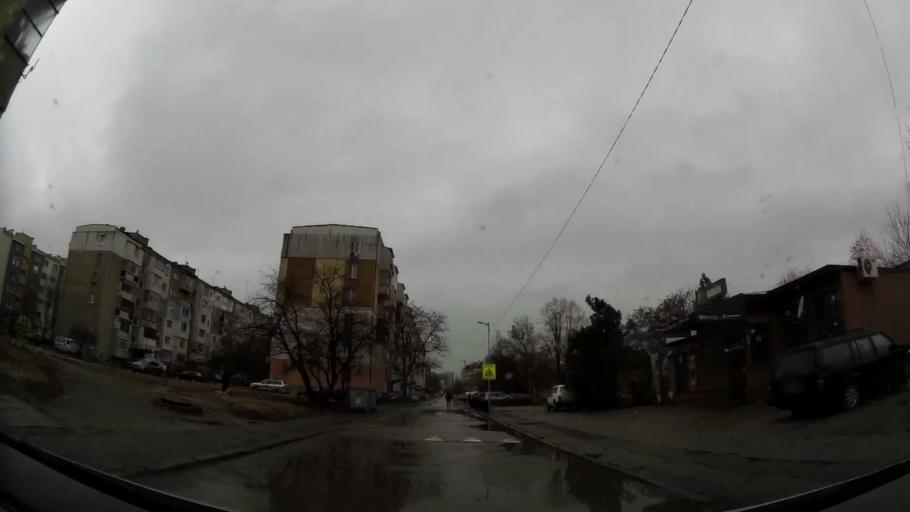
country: BG
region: Sofia-Capital
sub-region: Stolichna Obshtina
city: Sofia
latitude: 42.6663
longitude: 23.3975
